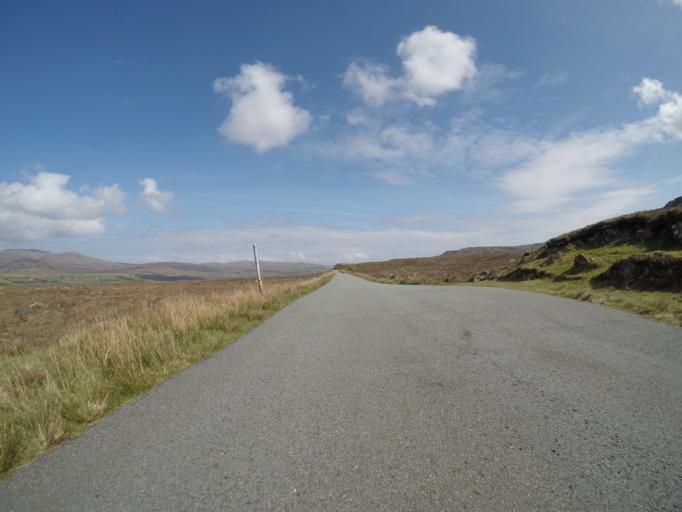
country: GB
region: Scotland
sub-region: Highland
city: Isle of Skye
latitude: 57.4226
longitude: -6.2721
